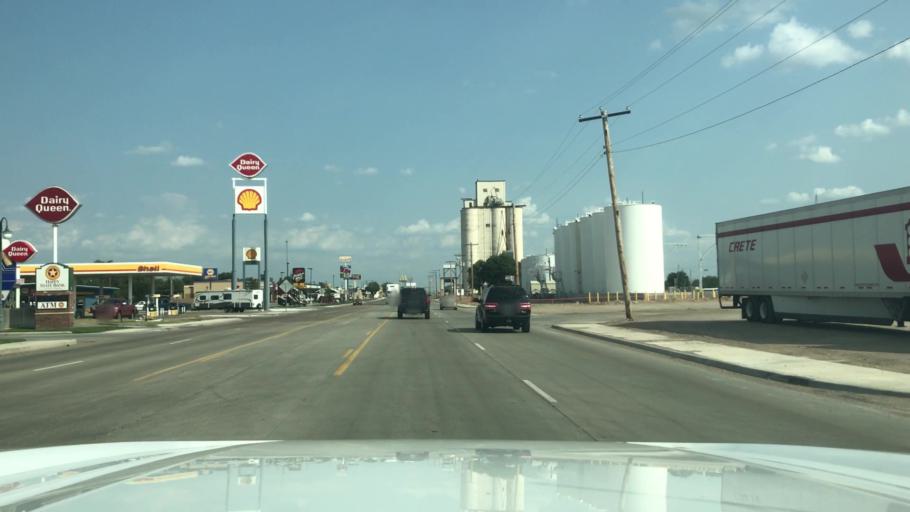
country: US
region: Texas
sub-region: Dallam County
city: Dalhart
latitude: 36.0640
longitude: -102.5196
